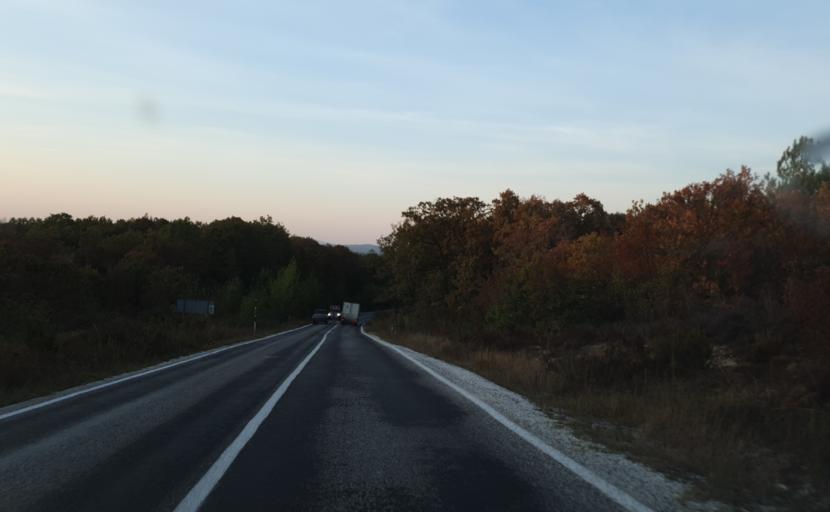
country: TR
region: Kirklareli
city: Igneada
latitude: 41.8690
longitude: 27.8861
